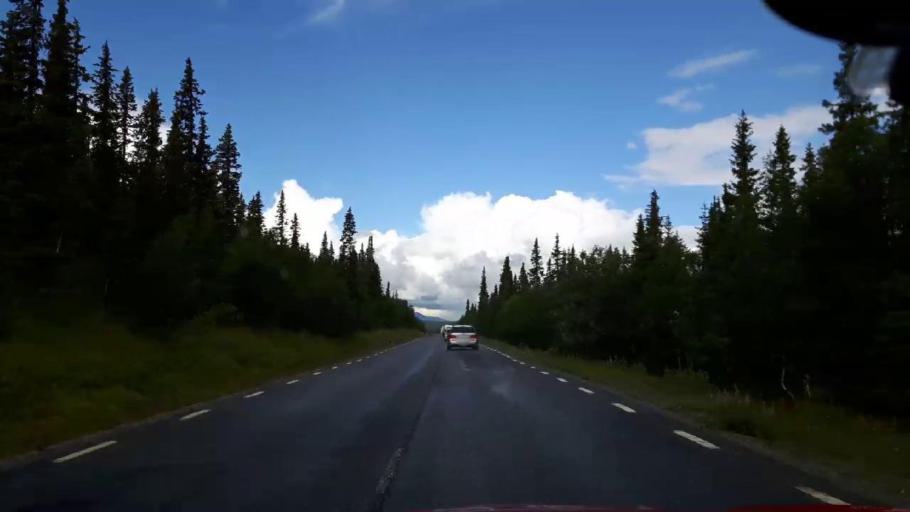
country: SE
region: Vaesterbotten
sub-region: Vilhelmina Kommun
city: Sjoberg
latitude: 65.0264
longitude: 15.1488
